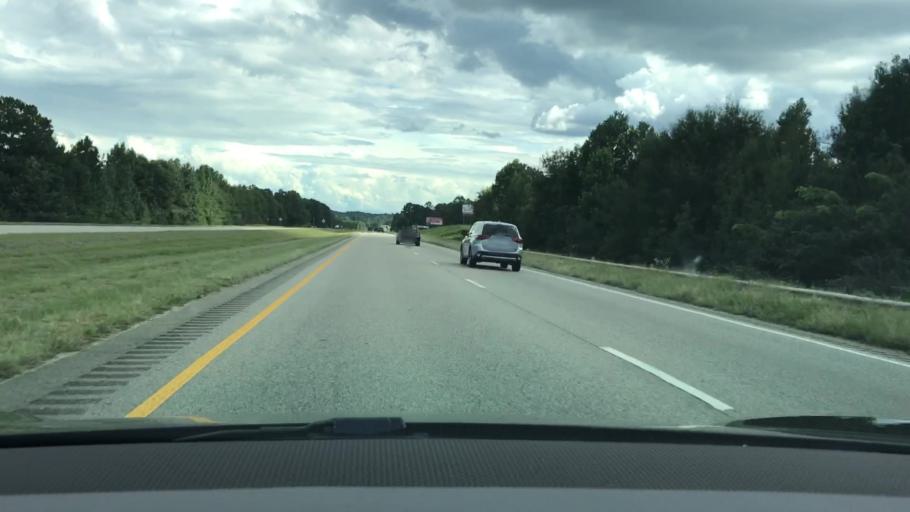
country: US
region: Alabama
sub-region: Pike County
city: Troy
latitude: 31.8614
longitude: -85.9986
